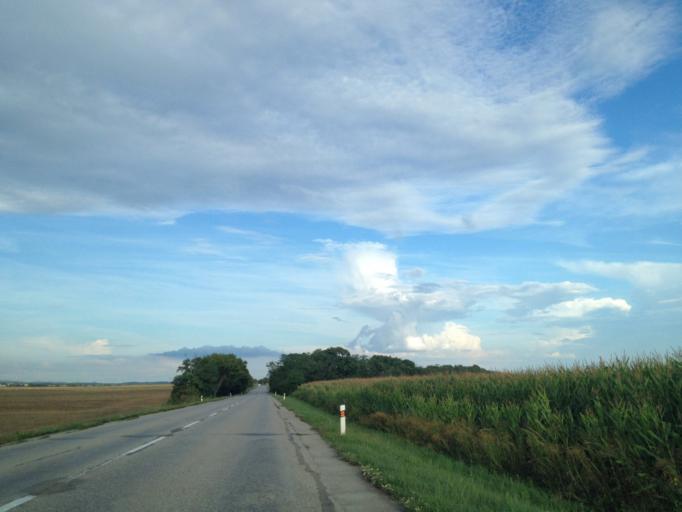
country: SK
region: Nitriansky
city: Svodin
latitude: 47.8999
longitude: 18.3625
